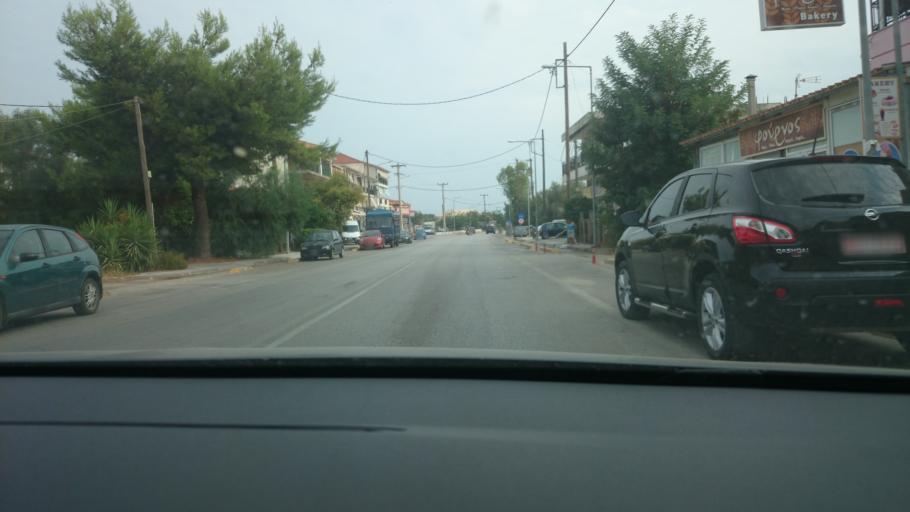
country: GR
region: Ionian Islands
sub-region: Lefkada
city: Lefkada
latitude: 38.8214
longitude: 20.7022
